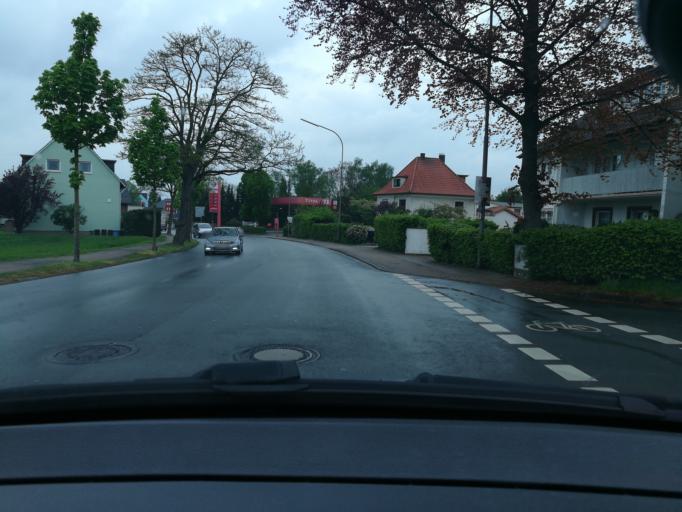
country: DE
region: North Rhine-Westphalia
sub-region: Regierungsbezirk Detmold
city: Herford
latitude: 52.1017
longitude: 8.6824
